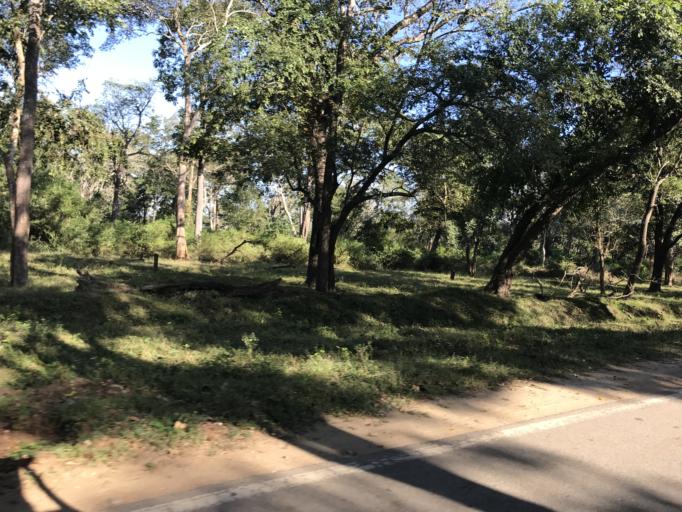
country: IN
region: Karnataka
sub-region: Mysore
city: Heggadadevankote
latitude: 11.9524
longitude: 76.2286
